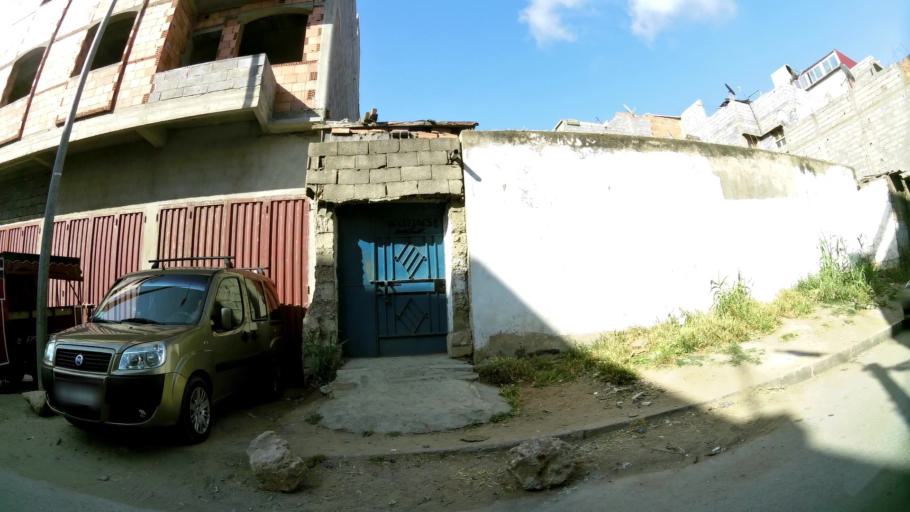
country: MA
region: Rabat-Sale-Zemmour-Zaer
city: Sale
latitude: 34.0621
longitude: -6.7715
